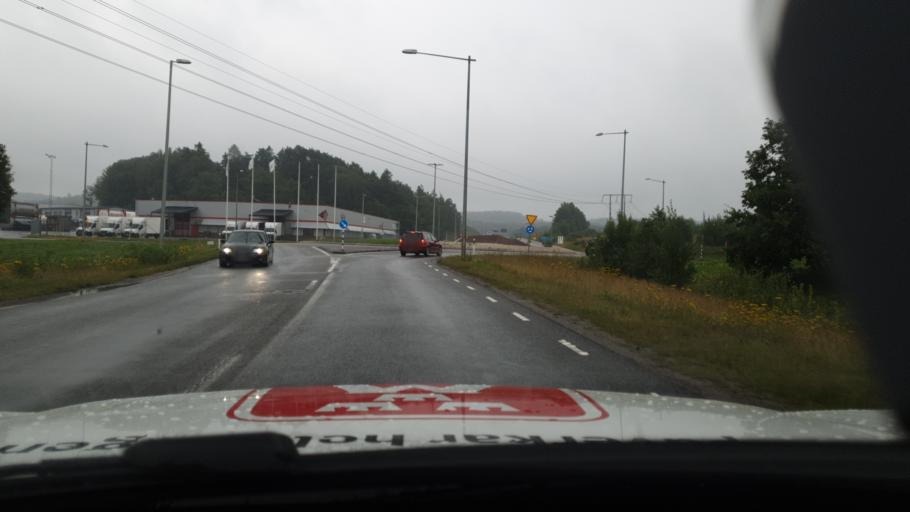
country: SE
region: Vaestra Goetaland
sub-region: Stenungsunds Kommun
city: Stenungsund
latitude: 58.0641
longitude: 11.8683
